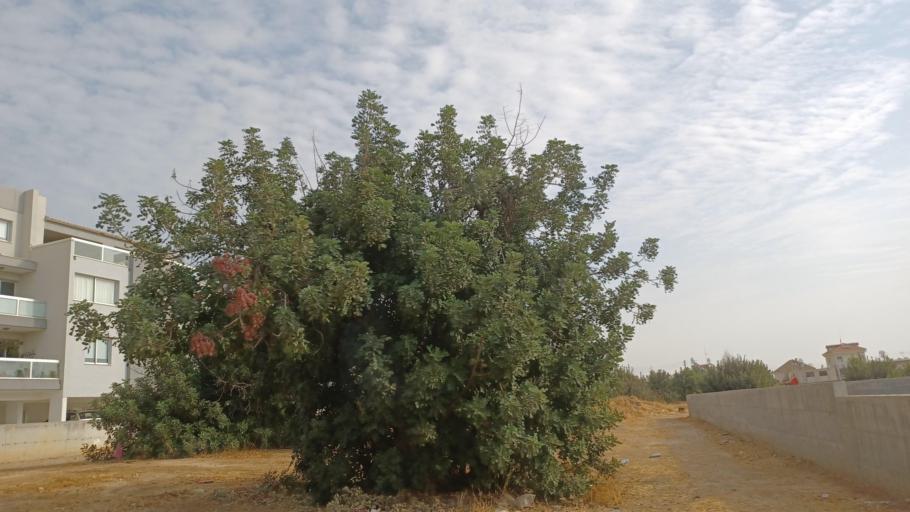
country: CY
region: Limassol
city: Ypsonas
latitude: 34.6986
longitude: 32.9568
